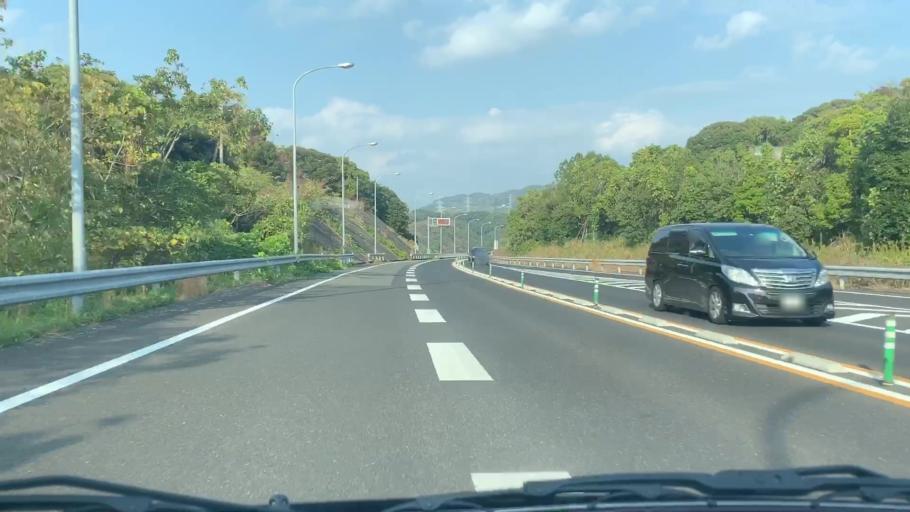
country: JP
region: Nagasaki
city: Sasebo
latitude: 33.0732
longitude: 129.7669
